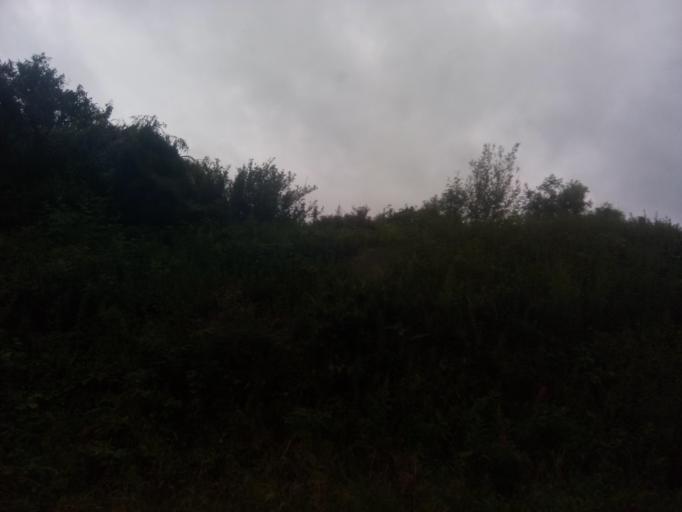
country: GB
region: England
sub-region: North Yorkshire
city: Settle
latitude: 54.0177
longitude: -2.2572
